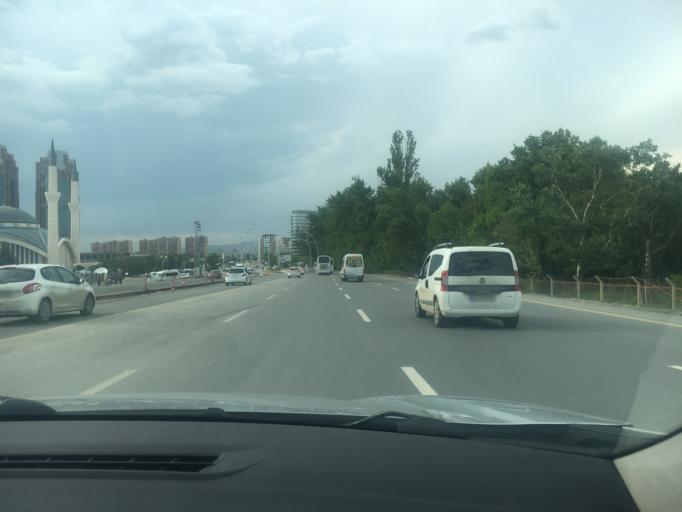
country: TR
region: Ankara
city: Batikent
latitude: 39.9039
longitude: 32.7653
